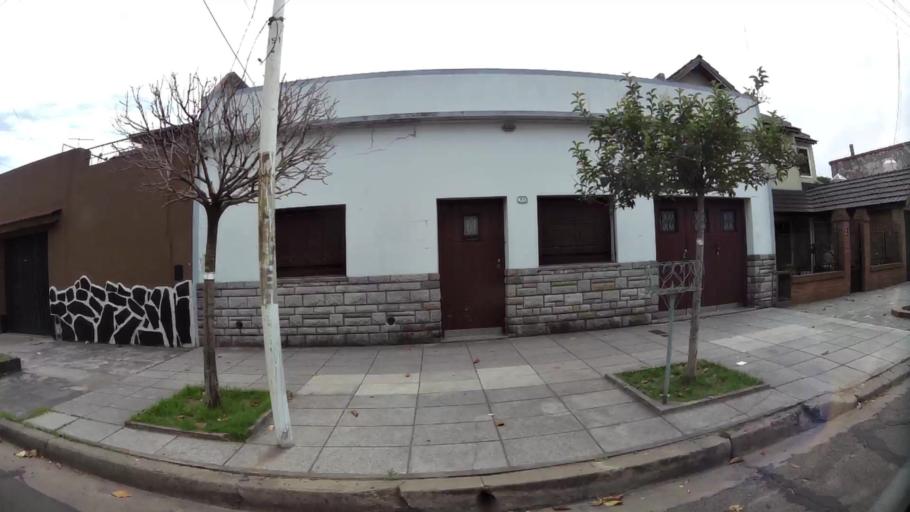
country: AR
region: Buenos Aires
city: San Justo
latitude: -34.6756
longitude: -58.5418
